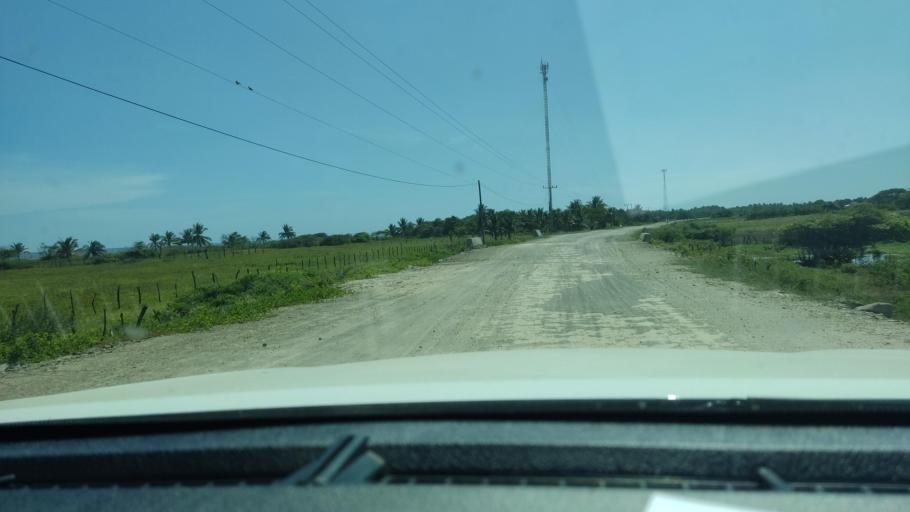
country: SV
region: Ahuachapan
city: San Francisco Menendez
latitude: 13.7663
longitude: -90.1751
